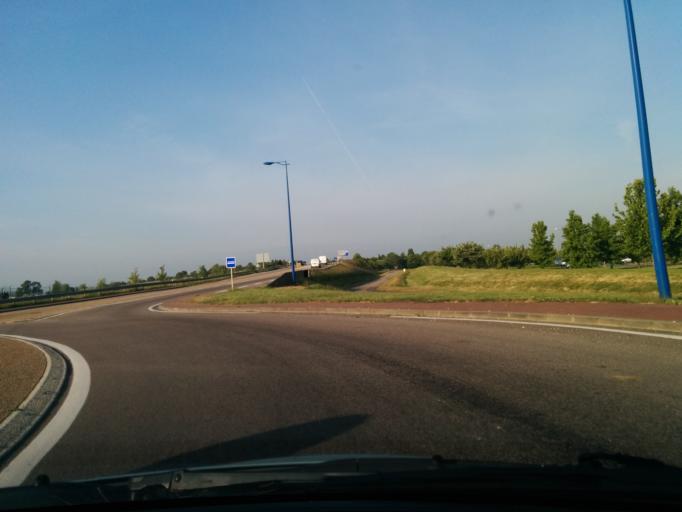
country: FR
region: Haute-Normandie
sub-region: Departement de l'Eure
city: Saint-Aubin-sur-Gaillon
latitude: 49.1391
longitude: 1.3162
